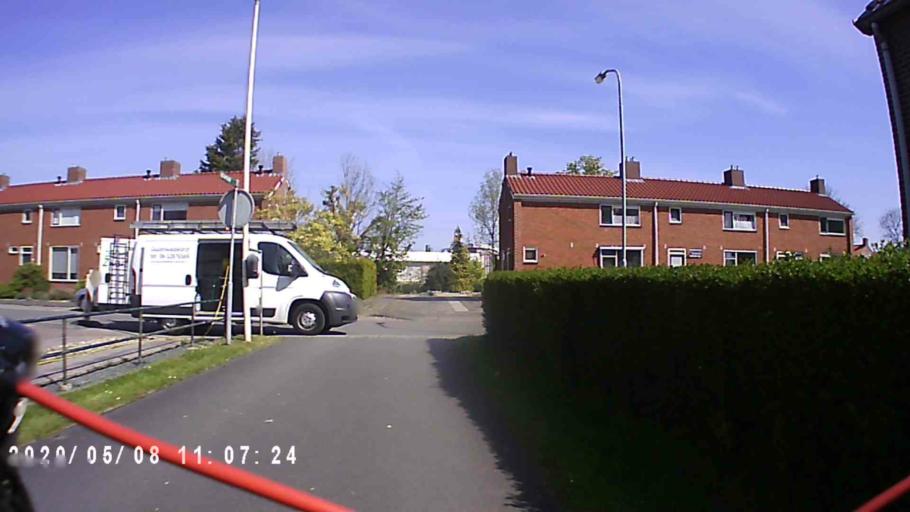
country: NL
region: Groningen
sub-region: Gemeente Bedum
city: Bedum
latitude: 53.3434
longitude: 6.6413
